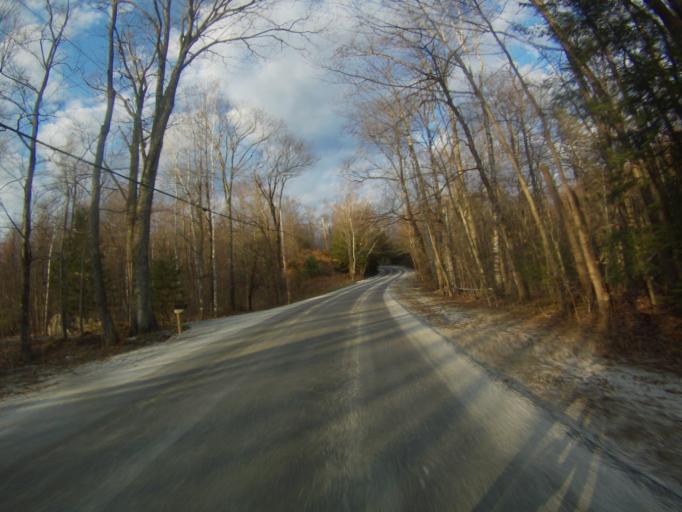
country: US
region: Vermont
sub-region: Rutland County
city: Brandon
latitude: 43.8525
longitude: -73.0163
